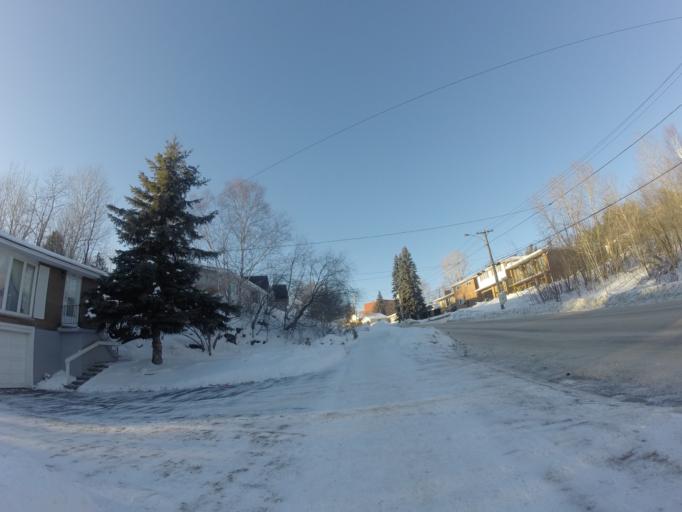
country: CA
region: Ontario
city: Greater Sudbury
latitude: 46.5066
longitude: -80.9985
